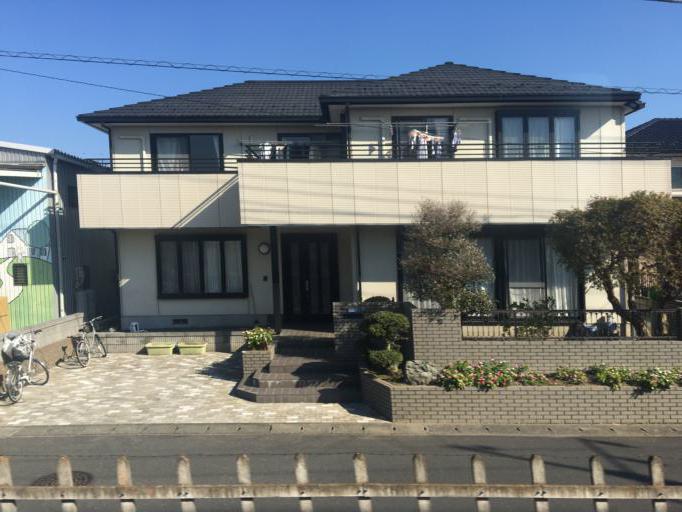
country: JP
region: Gunma
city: Kiryu
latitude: 36.3652
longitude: 139.3867
